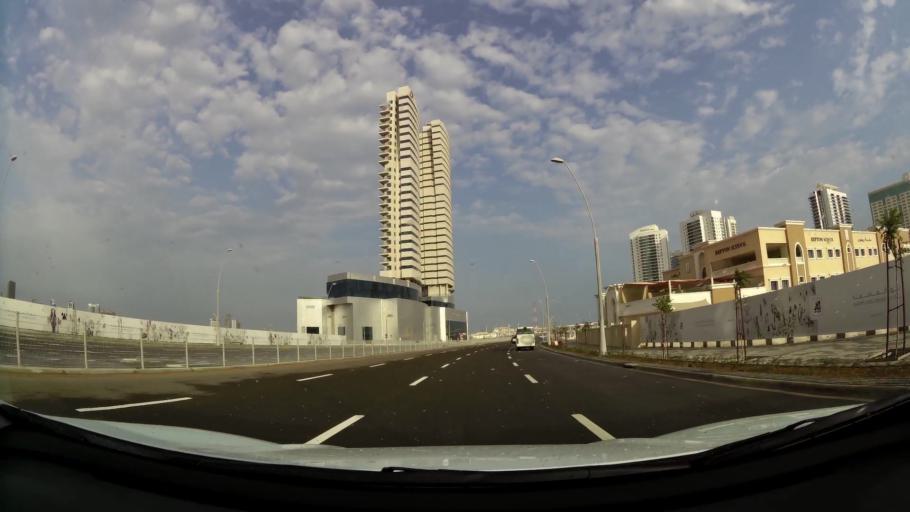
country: AE
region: Abu Dhabi
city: Abu Dhabi
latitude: 24.5066
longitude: 54.4069
